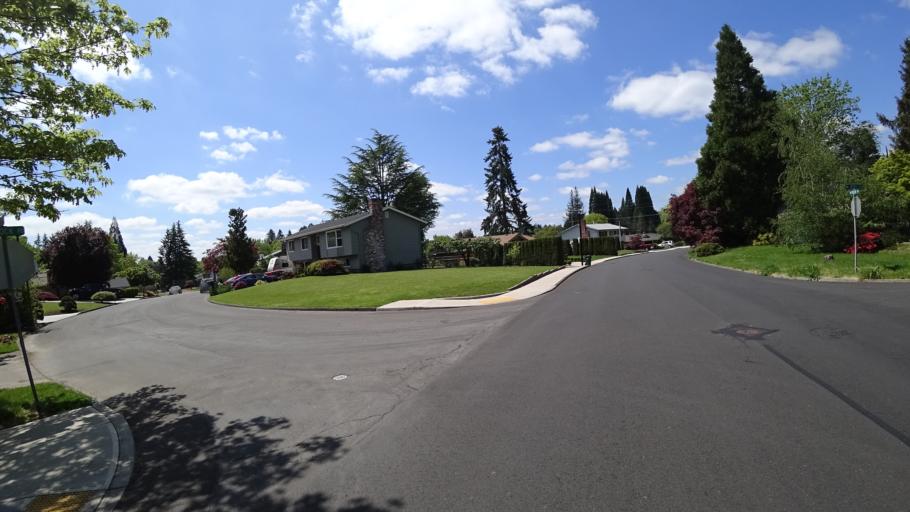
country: US
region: Oregon
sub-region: Washington County
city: Aloha
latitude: 45.5073
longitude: -122.9002
